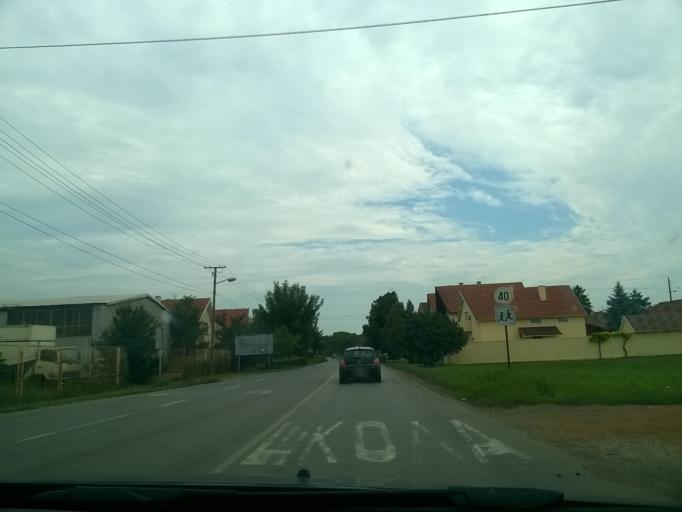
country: RS
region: Autonomna Pokrajina Vojvodina
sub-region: Srednjebanatski Okrug
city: Zrenjanin
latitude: 45.3957
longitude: 20.3932
